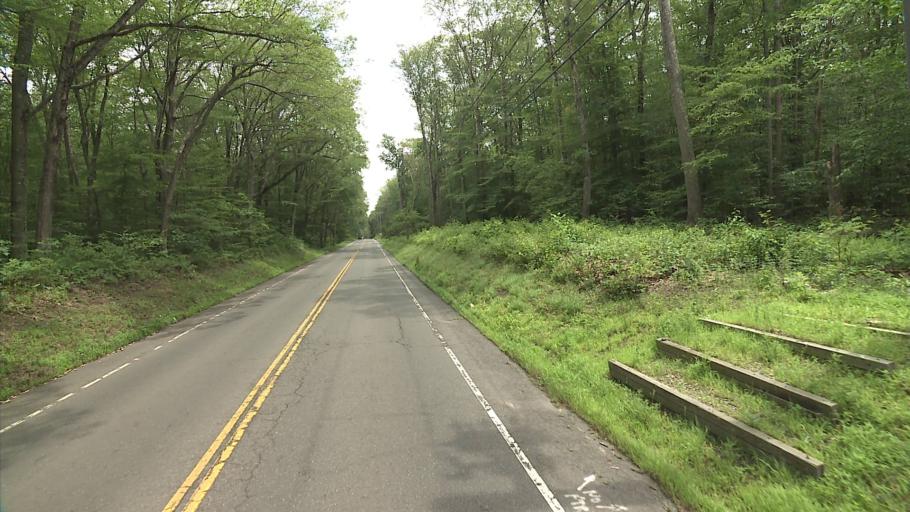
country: US
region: Connecticut
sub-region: Middlesex County
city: Chester Center
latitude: 41.3584
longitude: -72.5170
